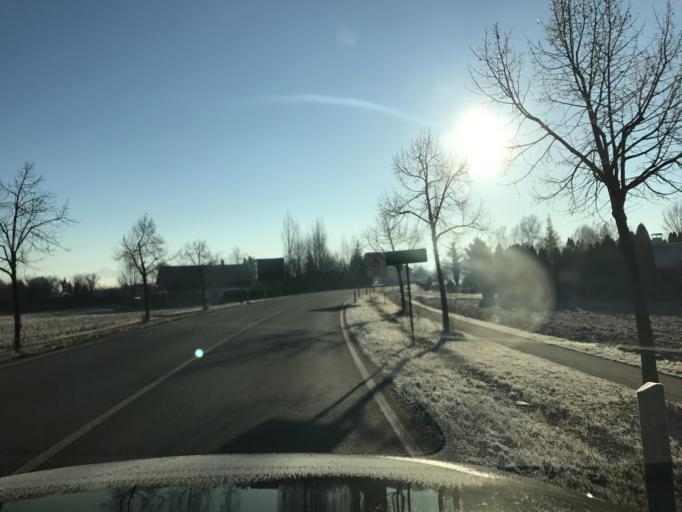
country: DE
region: Bavaria
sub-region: Upper Bavaria
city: Bad Aibling
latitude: 47.8494
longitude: 12.0177
